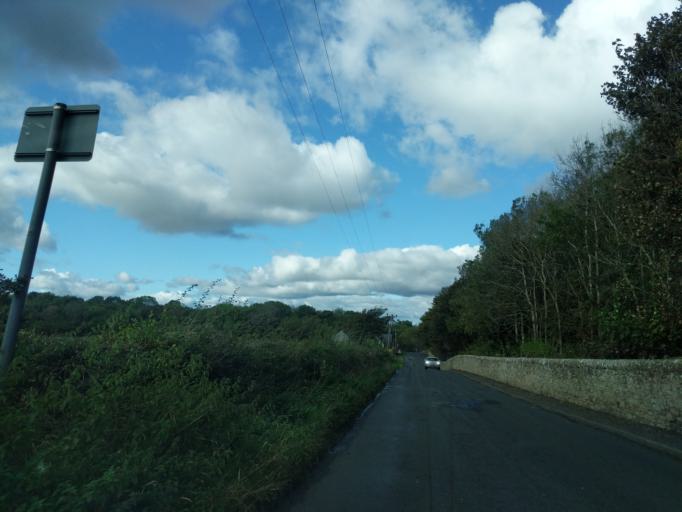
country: GB
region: Scotland
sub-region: Edinburgh
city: Currie
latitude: 55.9078
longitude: -3.3302
